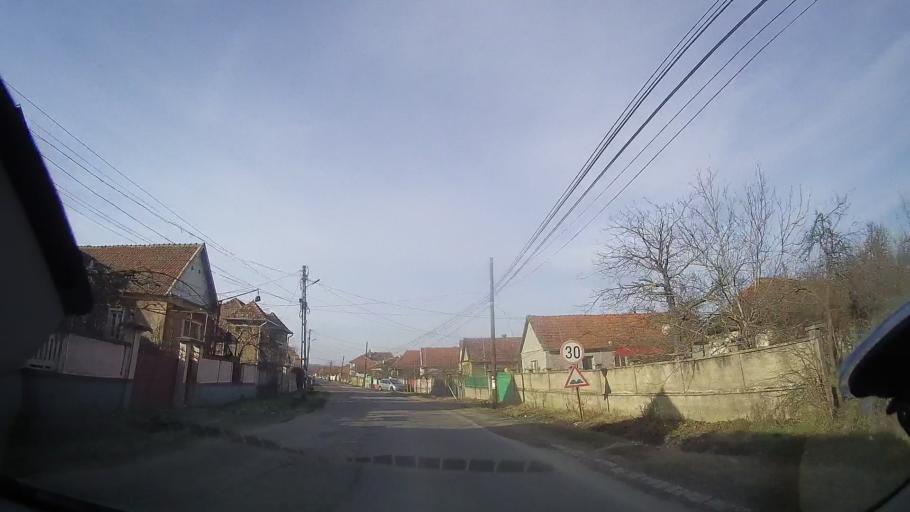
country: RO
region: Bihor
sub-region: Comuna Brusturi
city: Brusturi
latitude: 47.1583
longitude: 22.2369
